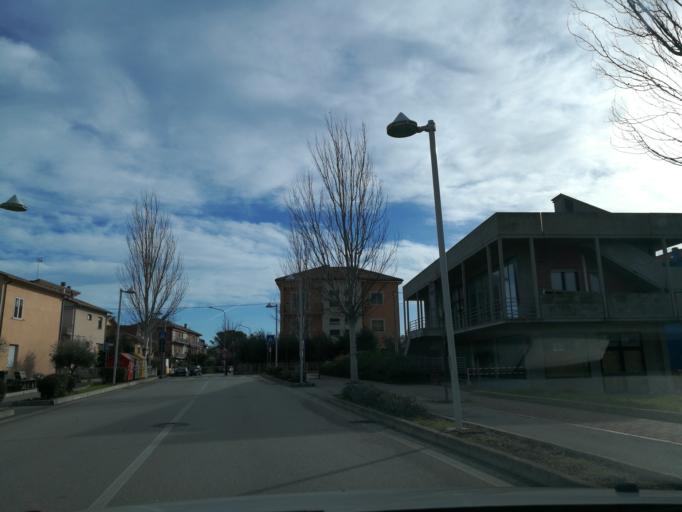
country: IT
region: The Marches
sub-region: Provincia di Pesaro e Urbino
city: Marotta
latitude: 43.7708
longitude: 13.1294
